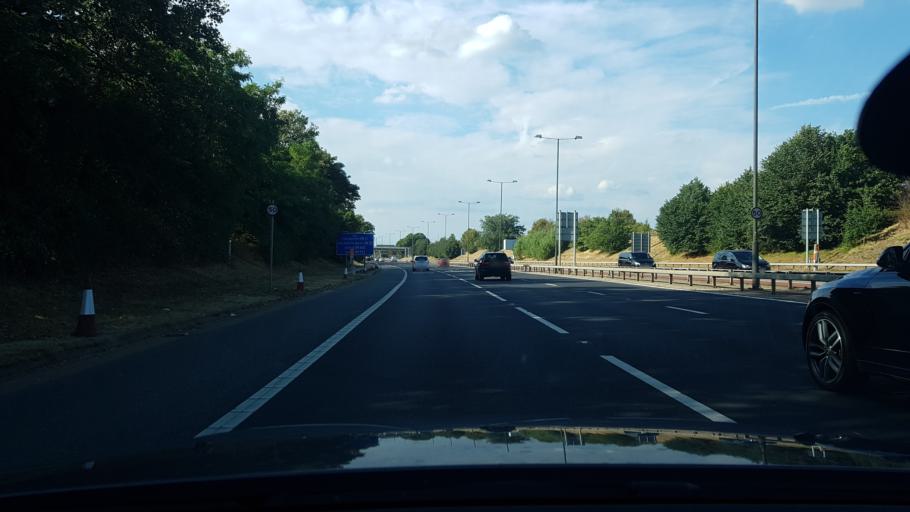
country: GB
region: England
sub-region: Greater London
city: West Drayton
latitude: 51.4853
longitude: -0.4528
